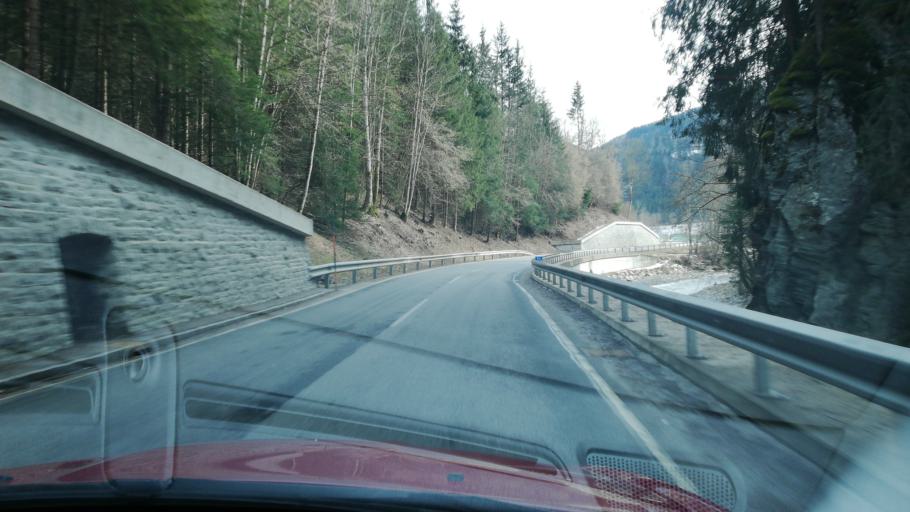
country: AT
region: Styria
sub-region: Politischer Bezirk Liezen
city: Irdning
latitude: 47.4840
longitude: 14.1129
